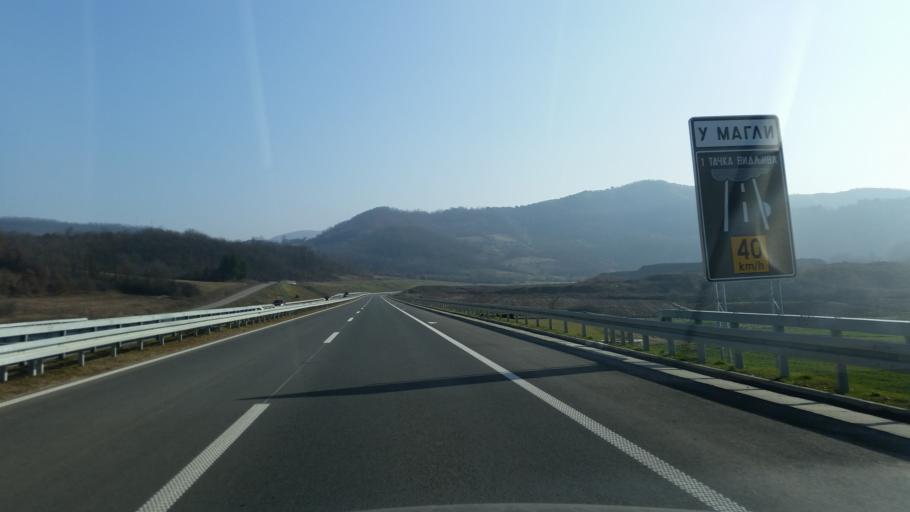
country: RS
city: Prislonica
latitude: 44.0024
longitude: 20.3959
